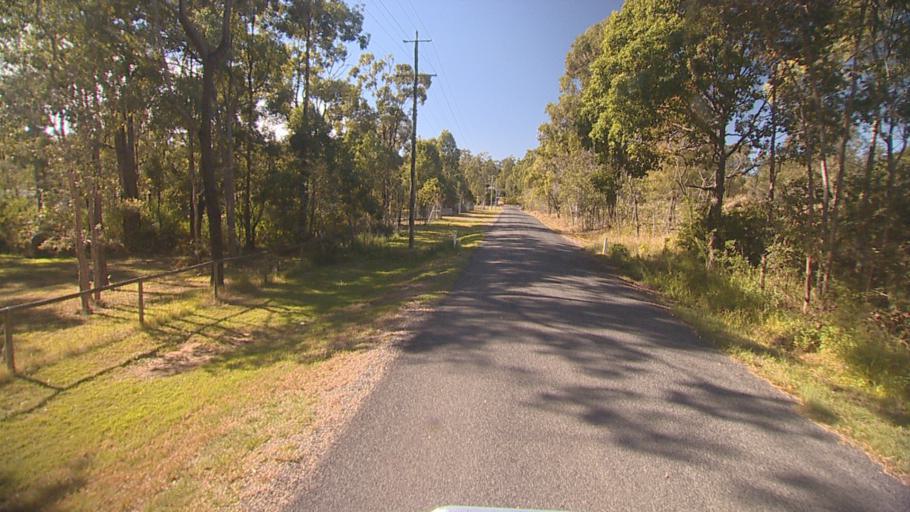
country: AU
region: Queensland
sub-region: Ipswich
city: Springfield Lakes
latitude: -27.6998
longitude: 152.9463
